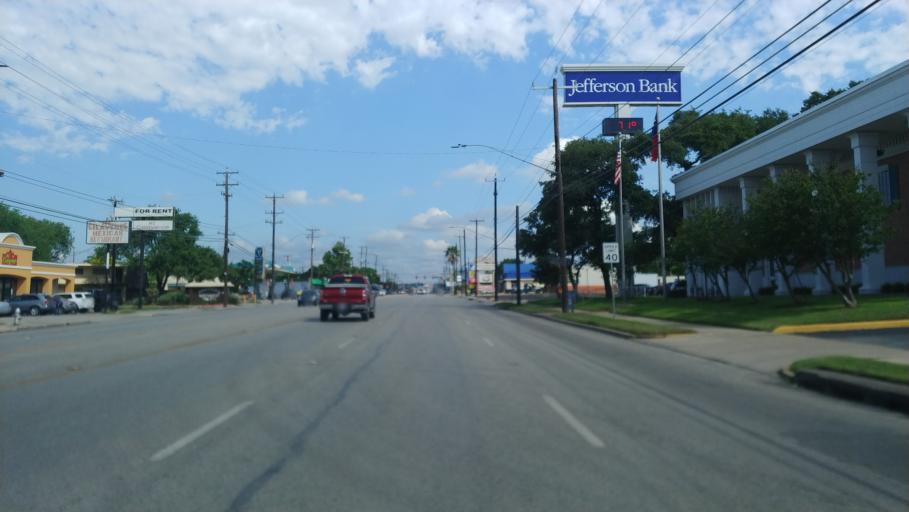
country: US
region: Texas
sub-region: Bexar County
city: Balcones Heights
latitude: 29.4702
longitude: -98.5316
